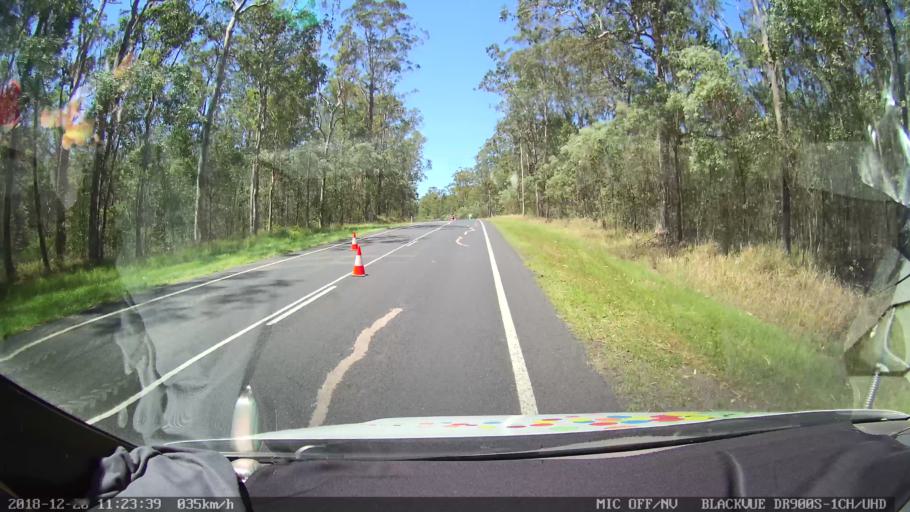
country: AU
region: New South Wales
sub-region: Richmond Valley
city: Casino
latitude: -29.0667
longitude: 153.0039
